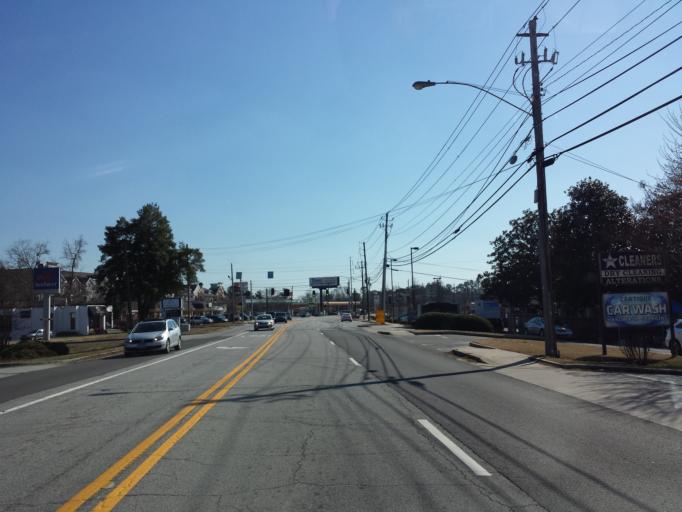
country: US
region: Georgia
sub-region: DeKalb County
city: Dunwoody
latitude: 33.9238
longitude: -84.3147
